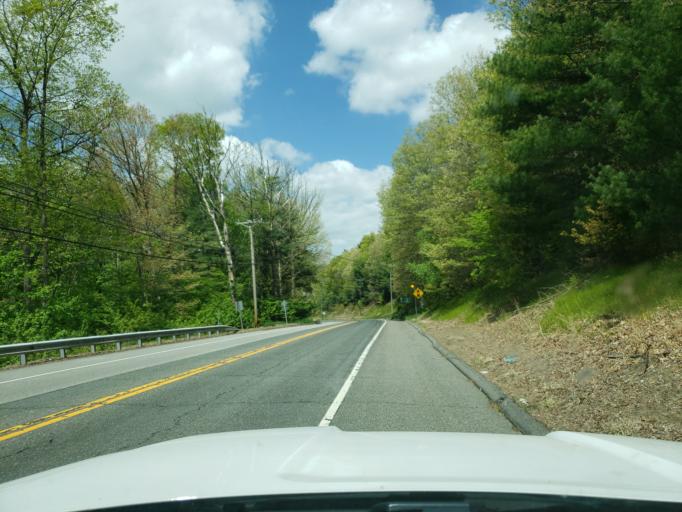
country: US
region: Connecticut
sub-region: Tolland County
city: Storrs
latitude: 41.8338
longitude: -72.3042
